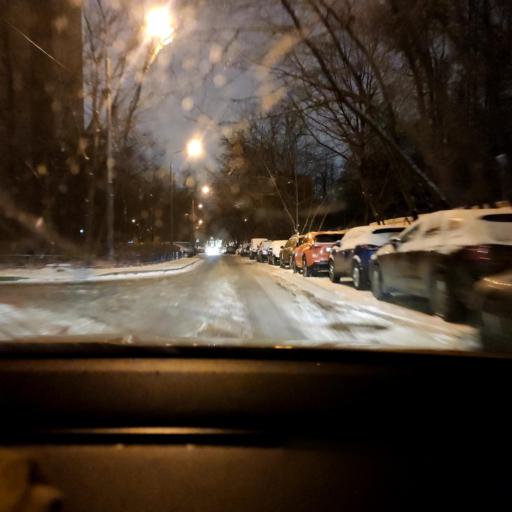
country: RU
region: Moskovskaya
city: Bol'shaya Setun'
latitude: 55.7351
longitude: 37.4372
